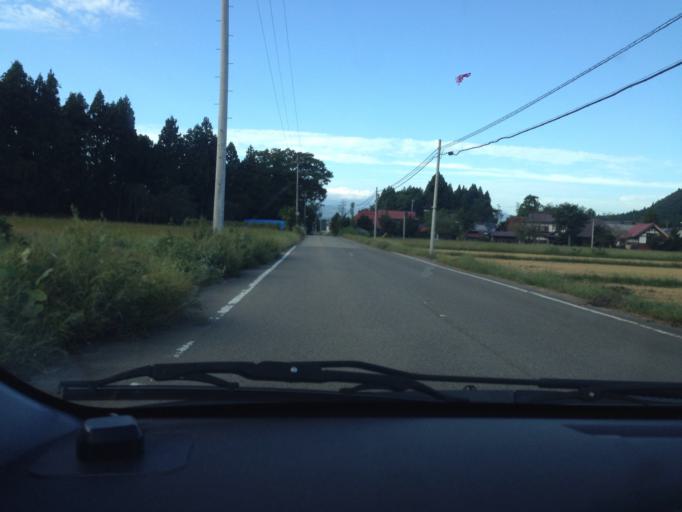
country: JP
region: Fukushima
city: Kitakata
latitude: 37.5800
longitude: 139.7711
